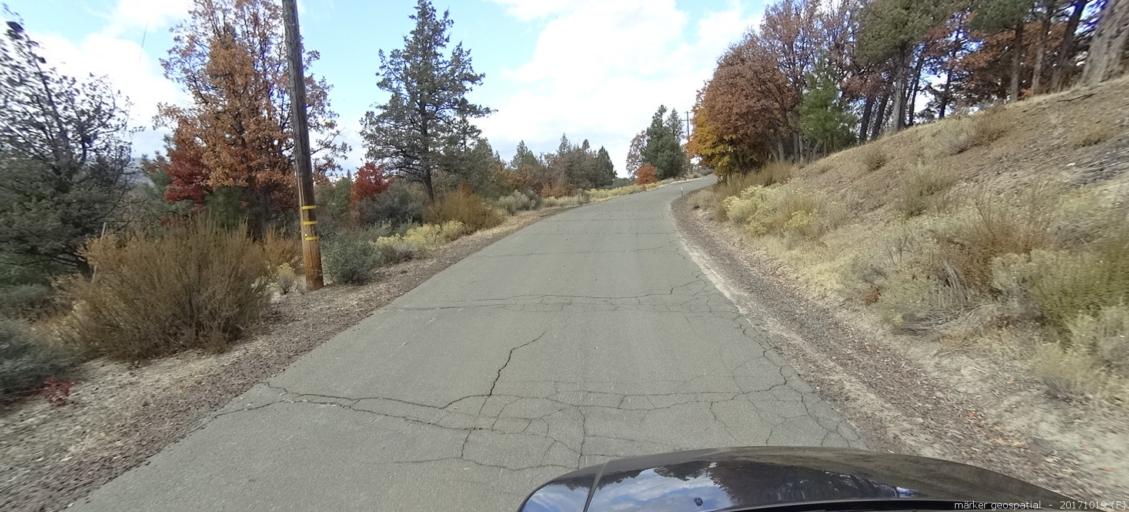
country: US
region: California
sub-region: Shasta County
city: Burney
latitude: 40.9735
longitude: -121.4460
